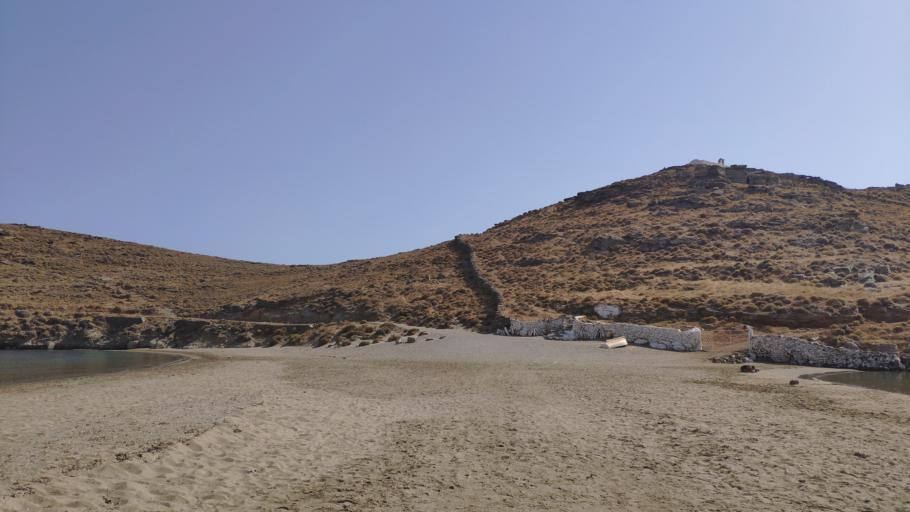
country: GR
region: South Aegean
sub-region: Nomos Kykladon
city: Kythnos
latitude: 37.4140
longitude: 24.3788
